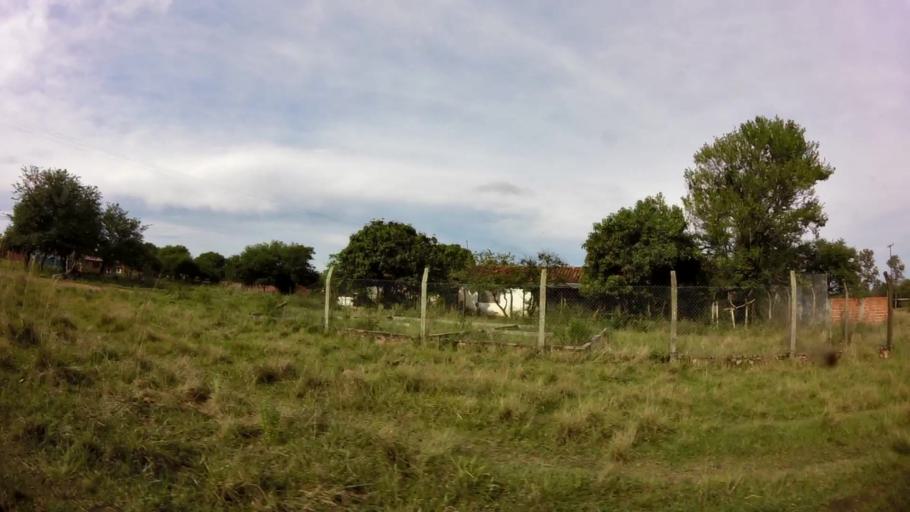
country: PY
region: Central
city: Limpio
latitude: -25.1740
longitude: -57.4942
